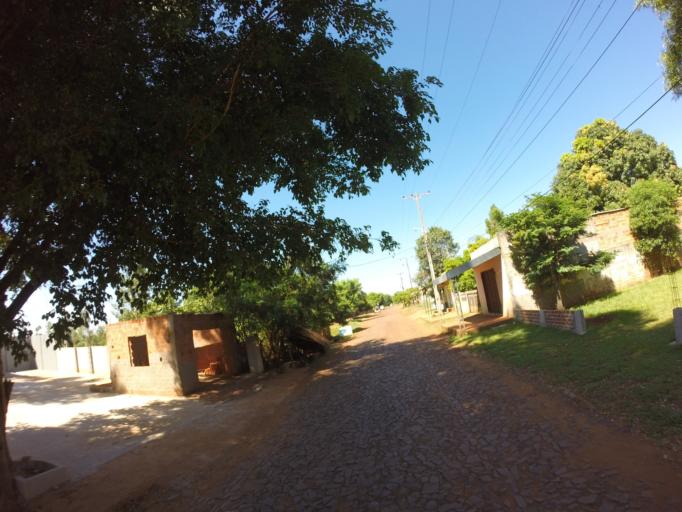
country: PY
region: Alto Parana
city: Ciudad del Este
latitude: -25.4316
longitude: -54.6449
